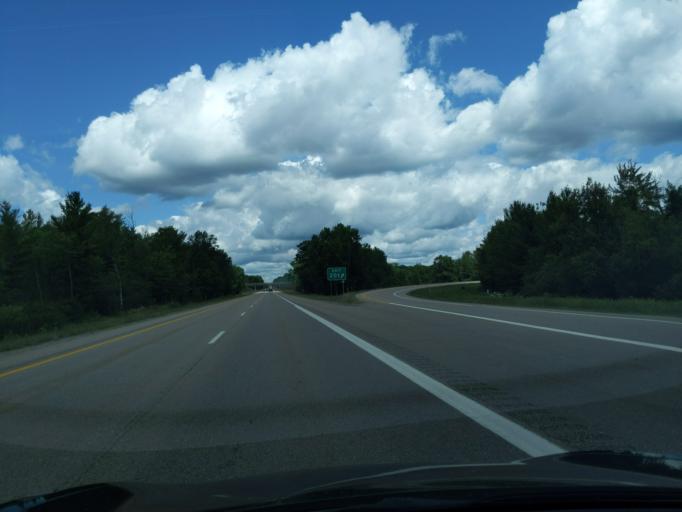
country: US
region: Michigan
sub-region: Roscommon County
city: Houghton Lake
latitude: 44.4313
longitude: -84.7885
